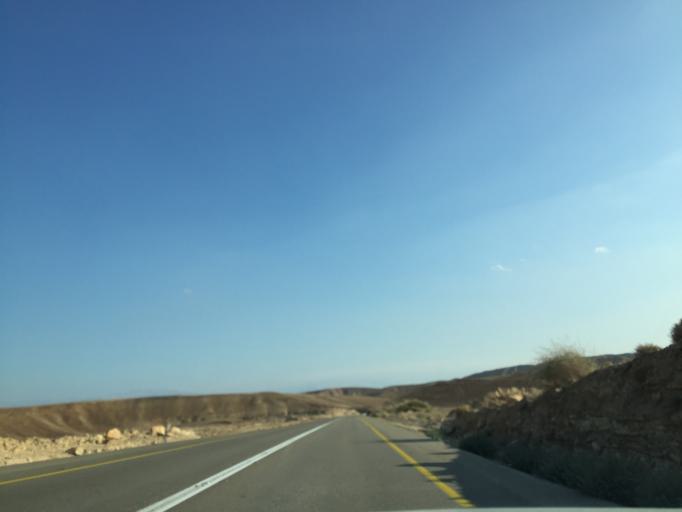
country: IL
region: Southern District
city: `En Boqeq
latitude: 31.1791
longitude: 35.2951
